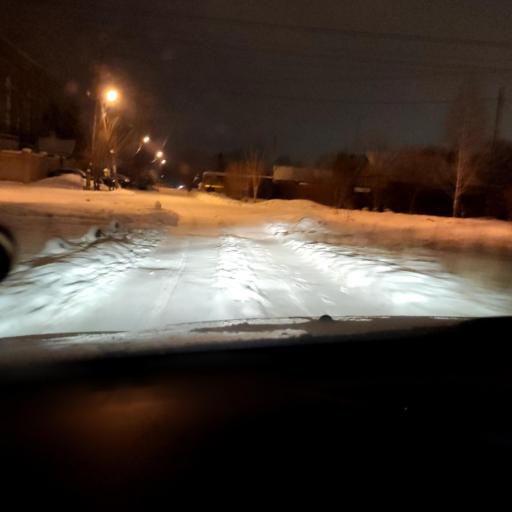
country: RU
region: Samara
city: Petra-Dubrava
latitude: 53.2444
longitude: 50.3228
